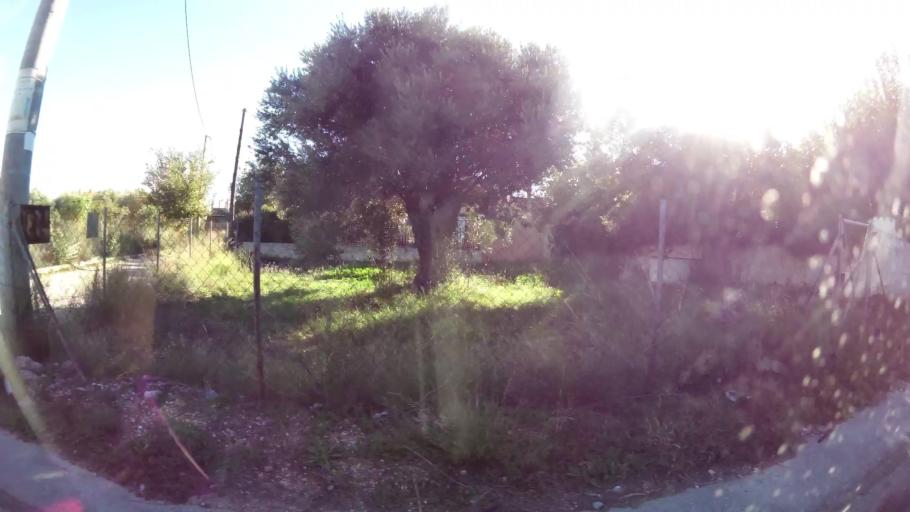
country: GR
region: Attica
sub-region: Nomarchia Anatolikis Attikis
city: Leondarion
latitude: 37.9741
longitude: 23.8512
